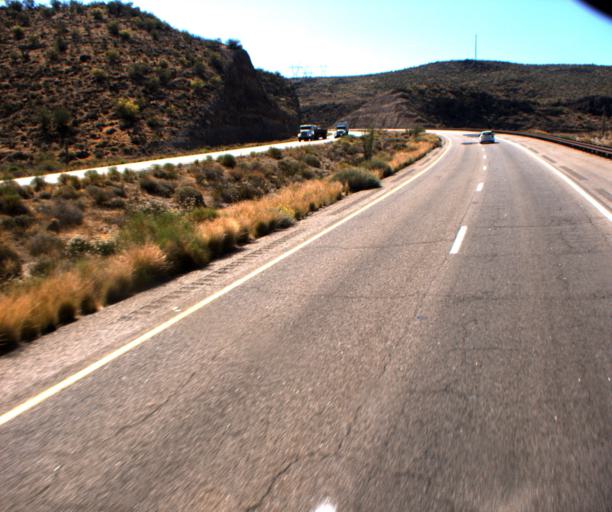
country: US
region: Arizona
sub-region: Yavapai County
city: Bagdad
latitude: 34.5742
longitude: -113.4890
